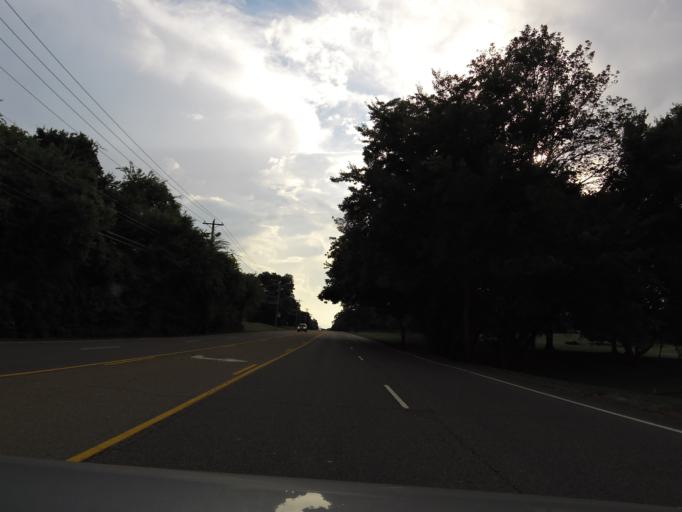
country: US
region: Tennessee
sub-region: Knox County
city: Farragut
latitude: 35.8673
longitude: -84.1894
